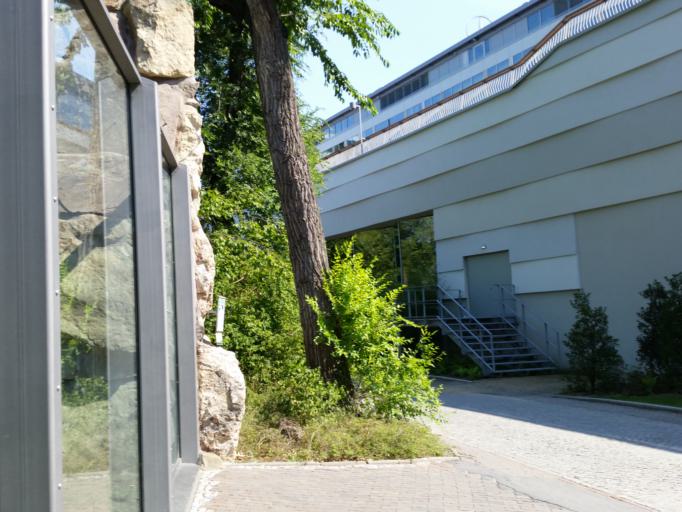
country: DE
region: Berlin
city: Hansaviertel
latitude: 52.5061
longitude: 13.3356
